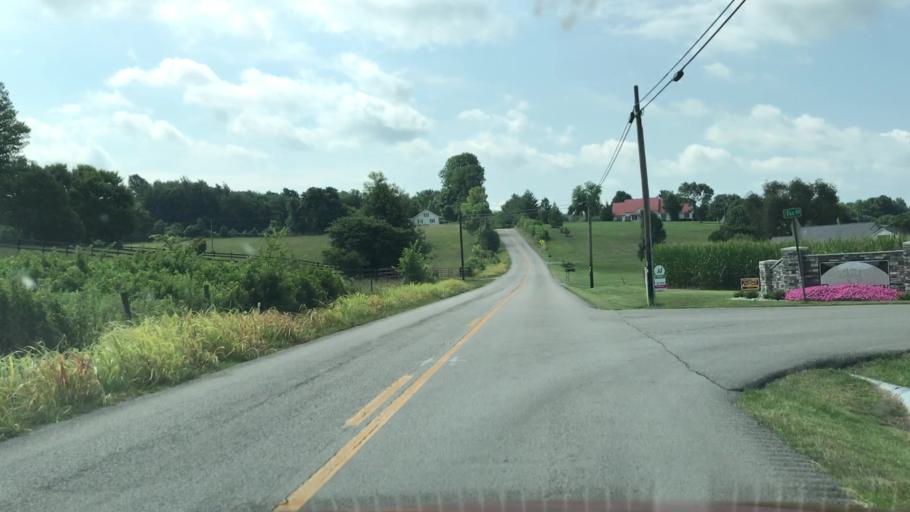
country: US
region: Kentucky
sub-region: Barren County
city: Glasgow
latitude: 36.9680
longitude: -85.8922
